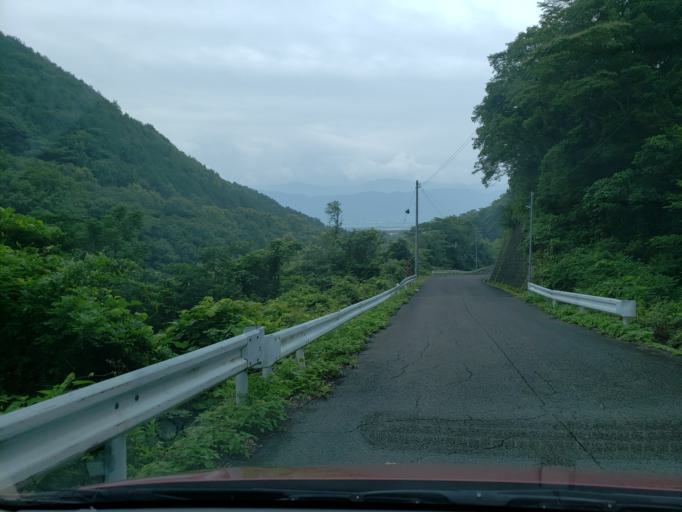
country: JP
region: Tokushima
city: Kamojimacho-jogejima
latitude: 34.1102
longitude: 134.2987
